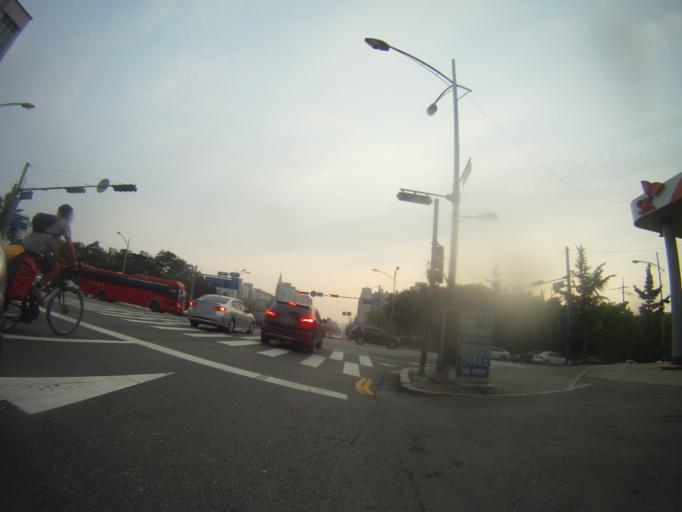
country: KR
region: Incheon
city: Incheon
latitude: 37.4575
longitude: 126.6920
